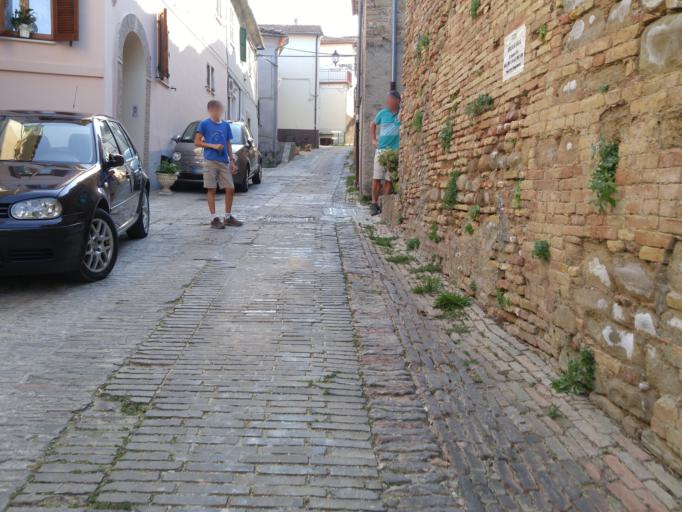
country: IT
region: Abruzzo
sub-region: Provincia di Pescara
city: Penne
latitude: 42.4599
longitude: 13.9246
